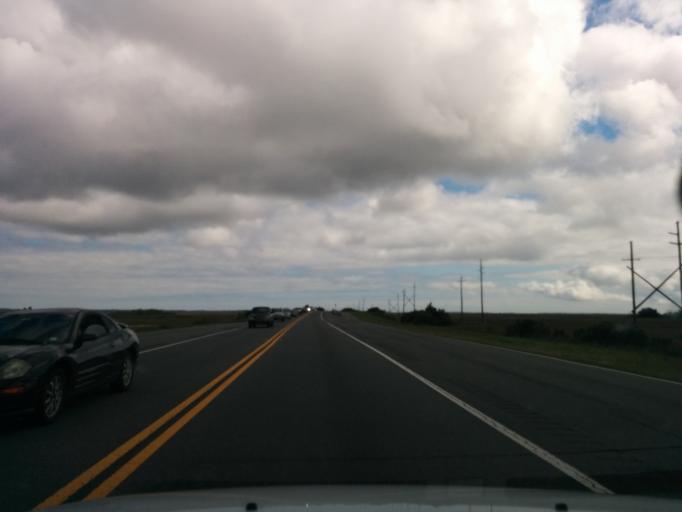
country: US
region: Georgia
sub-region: Glynn County
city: Brunswick
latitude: 31.0907
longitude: -81.4814
